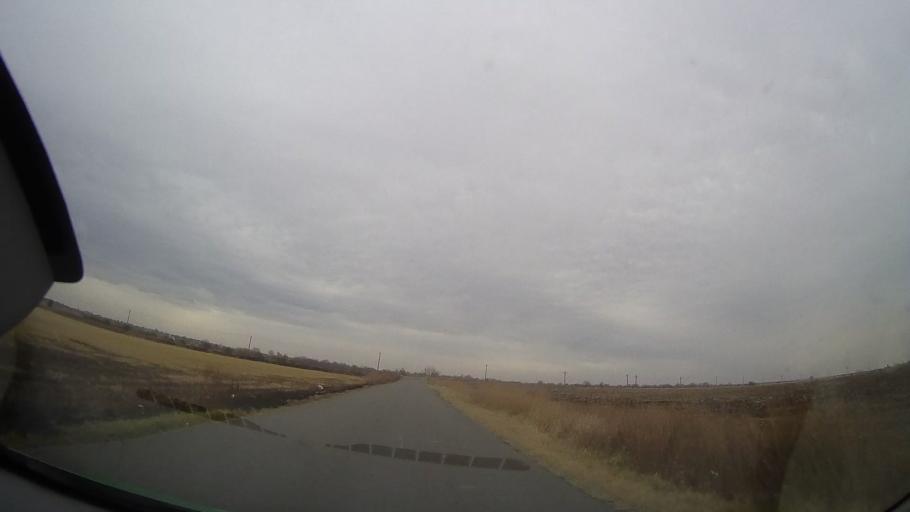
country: RO
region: Prahova
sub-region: Comuna Fantanele
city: Fantanele
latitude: 45.0093
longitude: 26.3555
